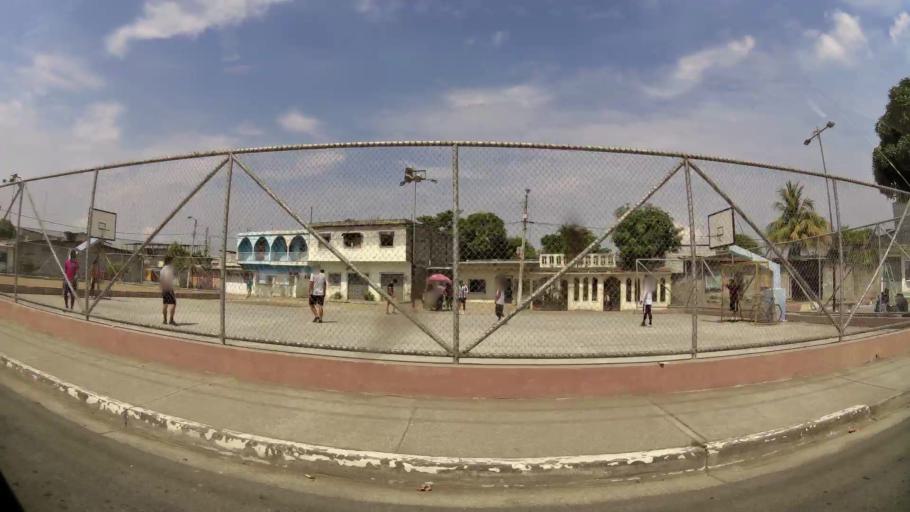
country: EC
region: Guayas
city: Guayaquil
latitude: -2.2626
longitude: -79.8715
